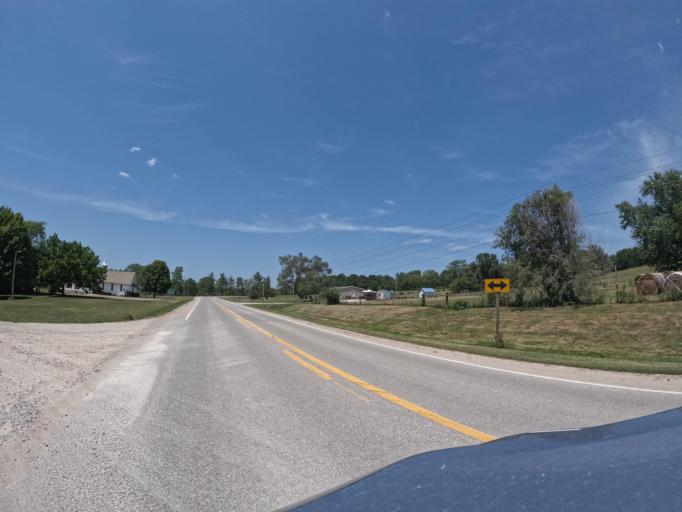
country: US
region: Iowa
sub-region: Henry County
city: Mount Pleasant
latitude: 40.9384
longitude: -91.6149
